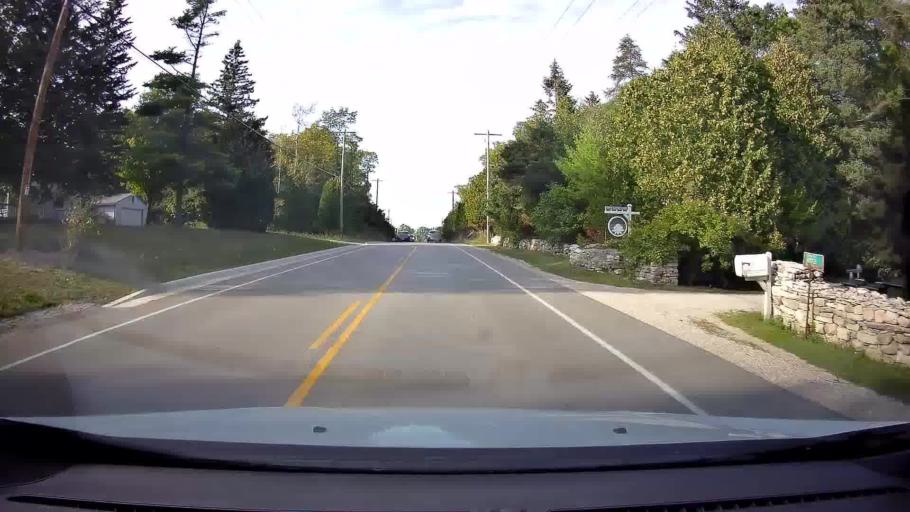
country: US
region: Wisconsin
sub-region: Door County
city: Sturgeon Bay
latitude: 45.1645
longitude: -87.1323
